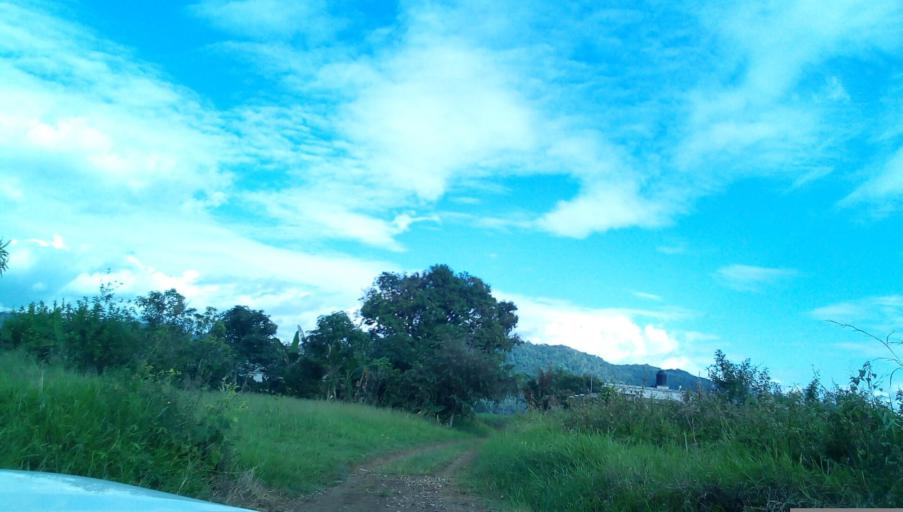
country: MX
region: Veracruz
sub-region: Amatlan de los Reyes
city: Centro de Readaptacion Social
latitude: 18.8263
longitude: -96.9227
